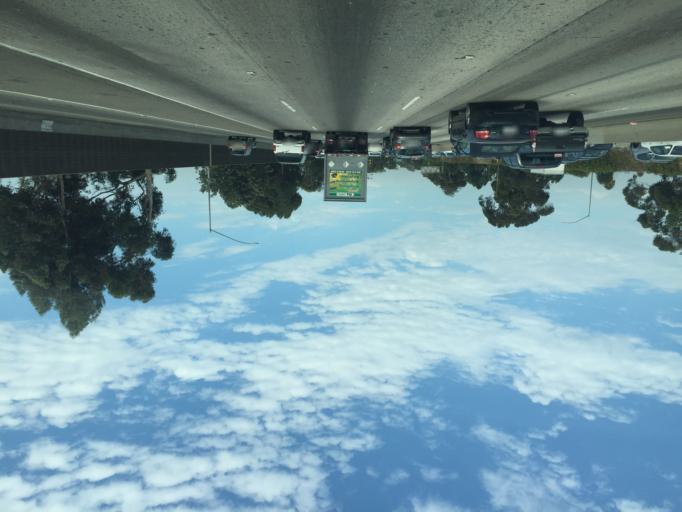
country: US
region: California
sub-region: Los Angeles County
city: Culver City
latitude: 34.0345
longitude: -118.3665
